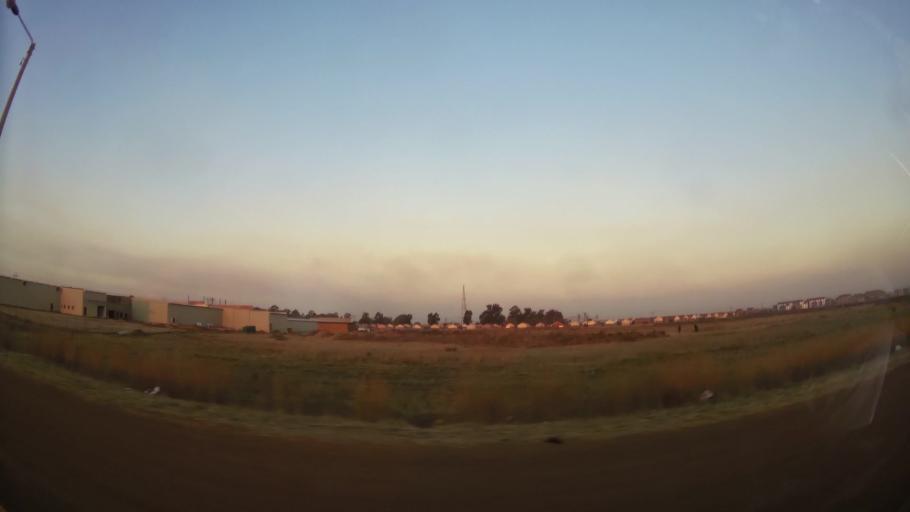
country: ZA
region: Gauteng
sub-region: Ekurhuleni Metropolitan Municipality
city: Springs
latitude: -26.3117
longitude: 28.4265
